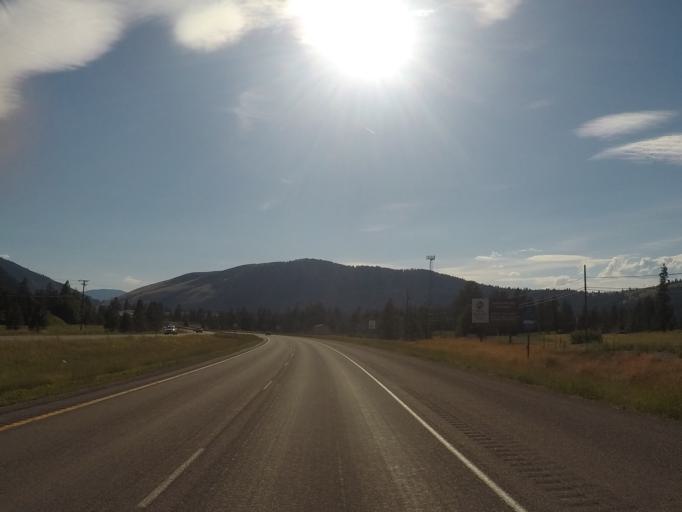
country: US
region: Montana
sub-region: Missoula County
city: Bonner-West Riverside
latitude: 46.8793
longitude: -113.9026
